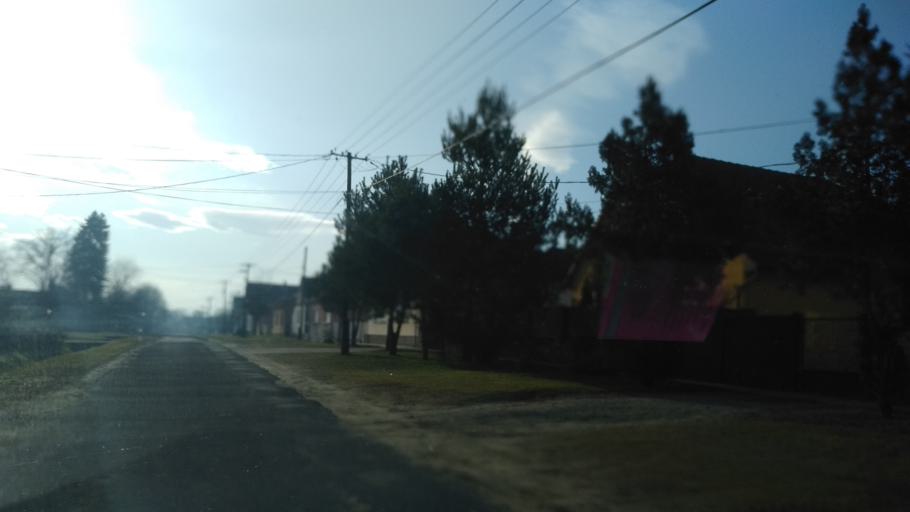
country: HU
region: Somogy
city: Barcs
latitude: 45.9638
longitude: 17.4778
